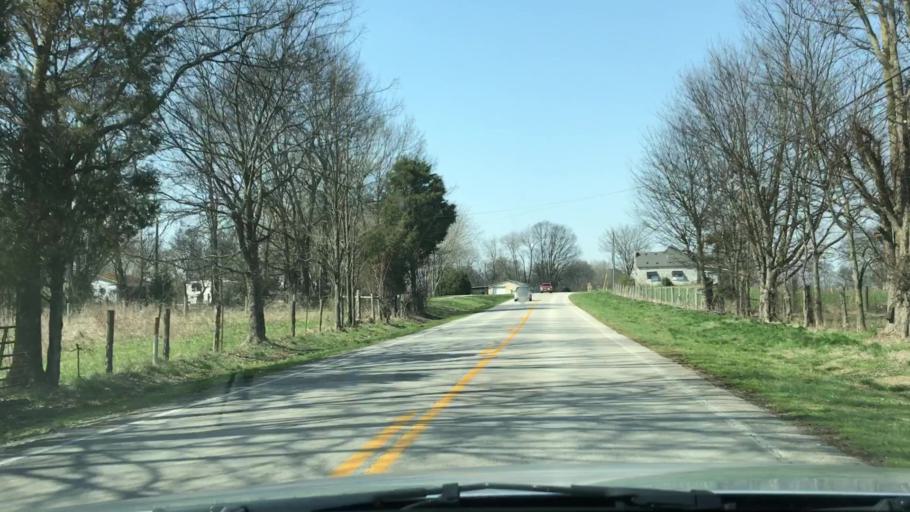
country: US
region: Kentucky
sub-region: Edmonson County
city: Brownsville
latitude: 37.0923
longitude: -86.1323
